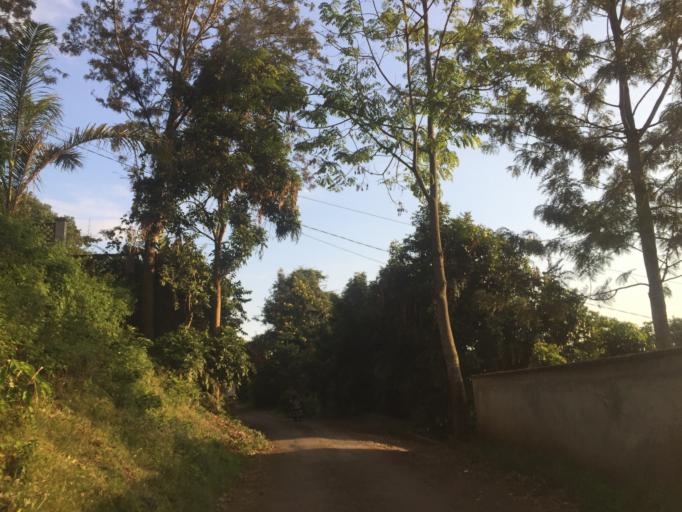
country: TZ
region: Arusha
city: Arusha
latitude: -3.3805
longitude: 36.7449
